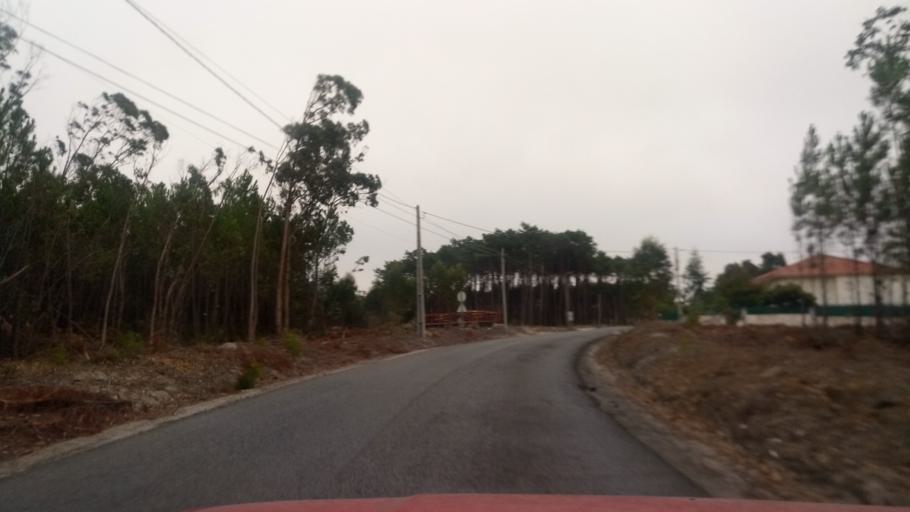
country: PT
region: Leiria
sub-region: Caldas da Rainha
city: Caldas da Rainha
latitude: 39.4466
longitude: -9.1690
